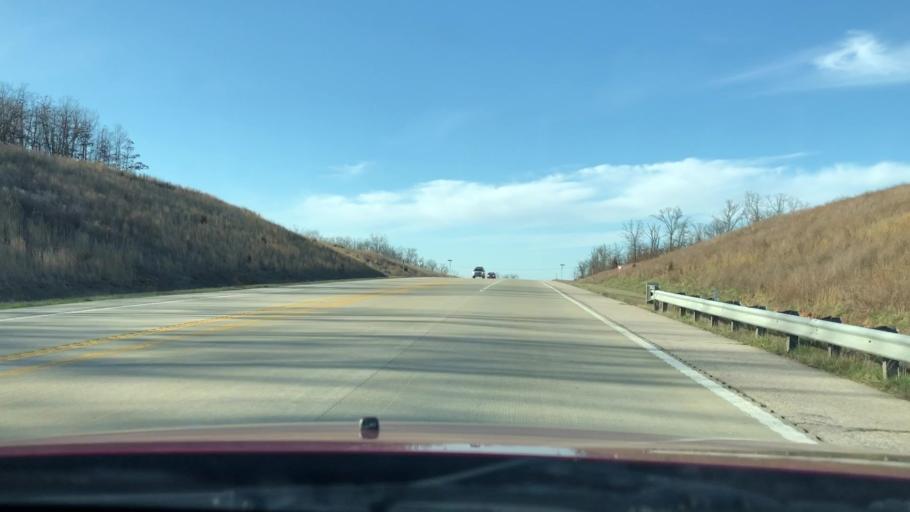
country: US
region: Missouri
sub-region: Camden County
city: Camdenton
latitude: 37.9341
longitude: -92.7147
